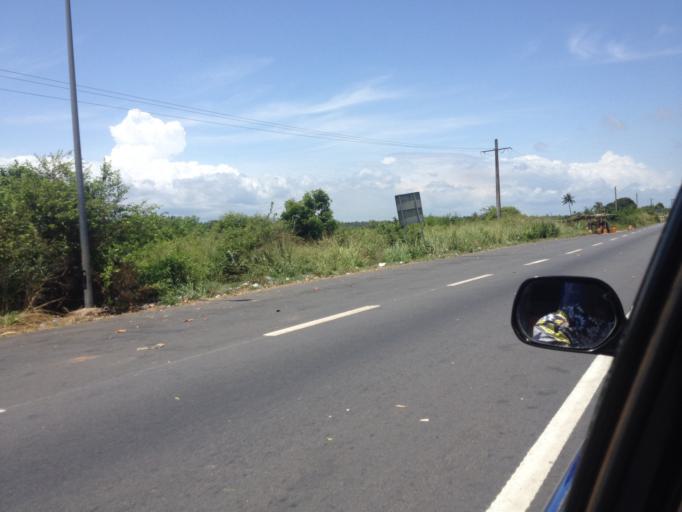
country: BJ
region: Mono
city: Grand-Popo
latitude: 6.2947
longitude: 1.8207
